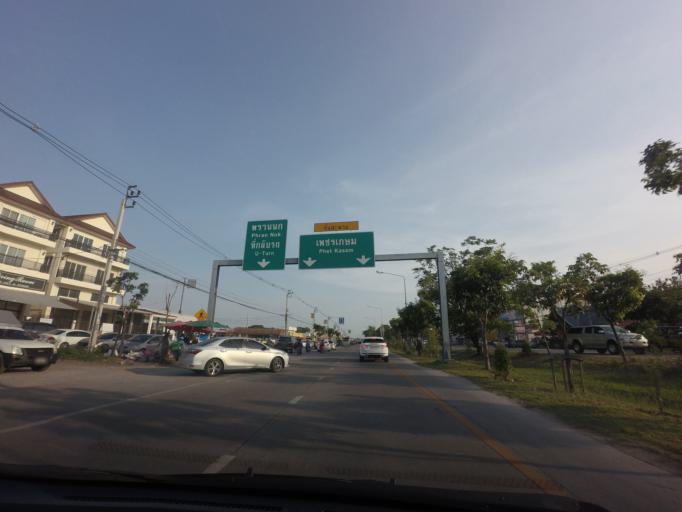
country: TH
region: Bangkok
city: Taling Chan
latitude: 13.7608
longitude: 100.4269
